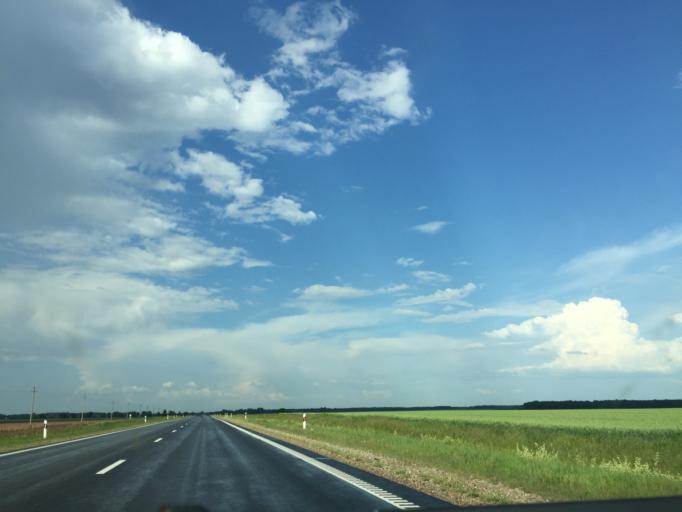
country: LT
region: Kauno apskritis
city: Kedainiai
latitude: 55.3082
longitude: 24.0962
